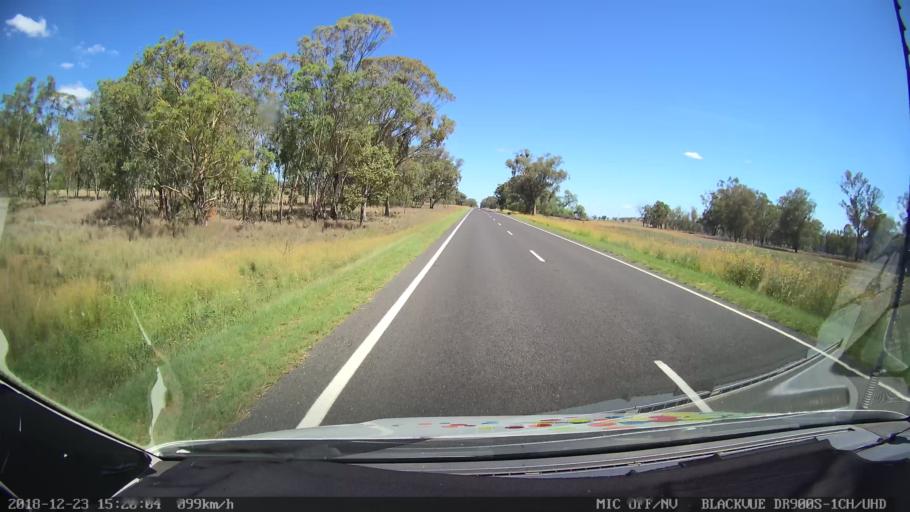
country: AU
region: New South Wales
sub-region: Tamworth Municipality
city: Manilla
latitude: -30.8377
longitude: 150.7872
